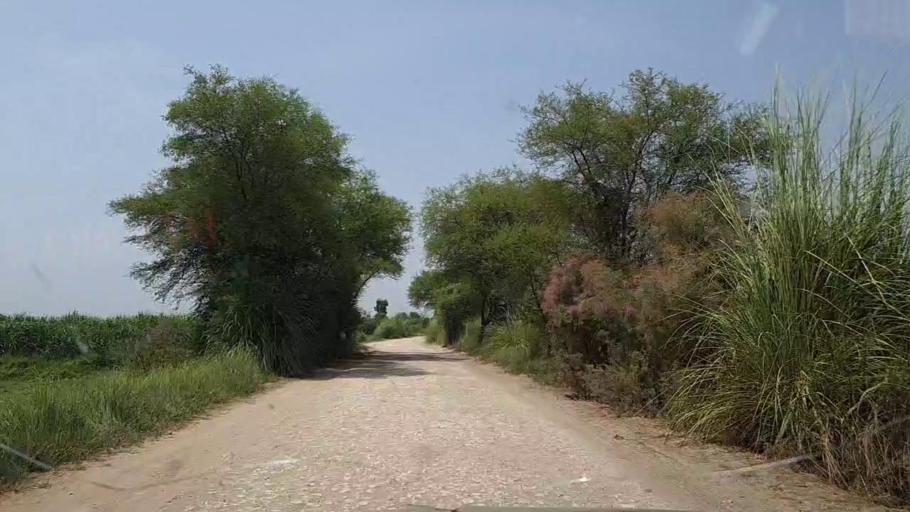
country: PK
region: Sindh
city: Ghotki
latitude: 28.0790
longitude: 69.3204
